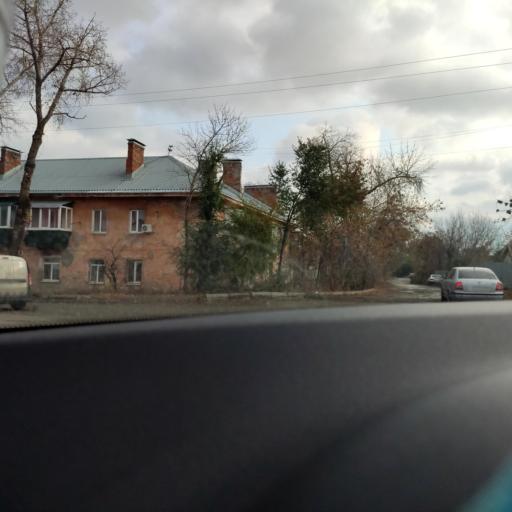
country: RU
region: Samara
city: Samara
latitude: 53.1737
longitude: 50.1724
